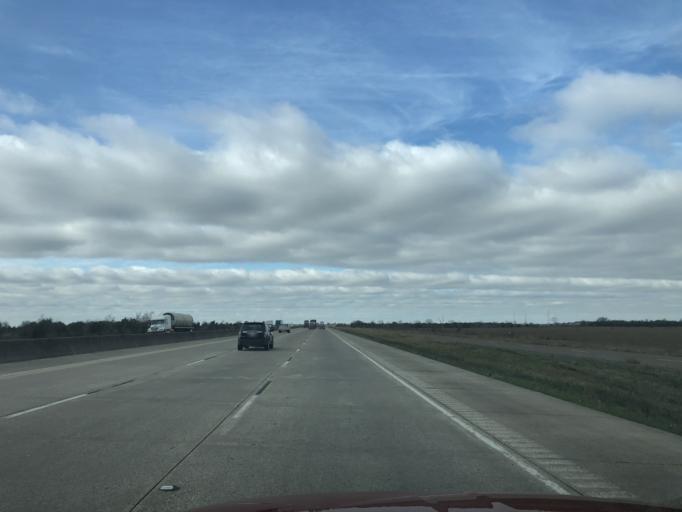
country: US
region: Texas
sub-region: Chambers County
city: Winnie
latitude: 29.8288
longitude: -94.4610
